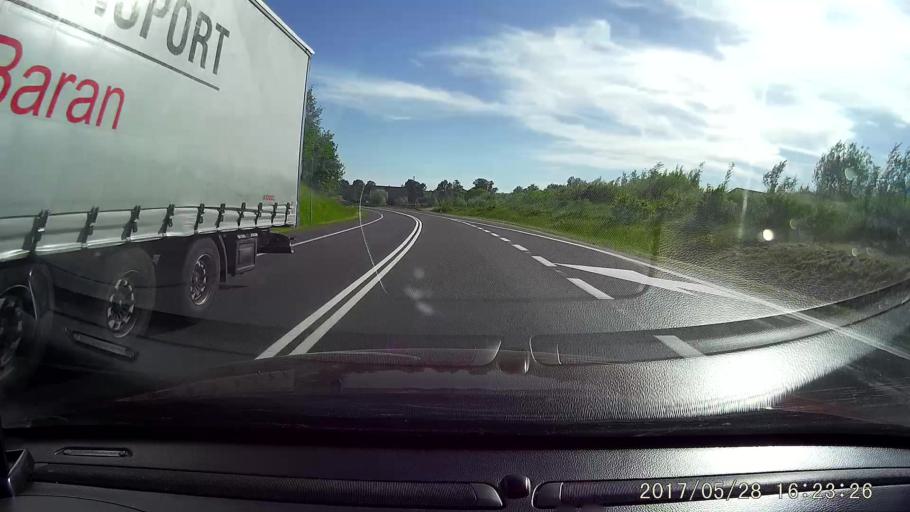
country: PL
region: Lower Silesian Voivodeship
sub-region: Powiat zgorzelecki
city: Lagow
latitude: 51.1802
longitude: 15.0340
